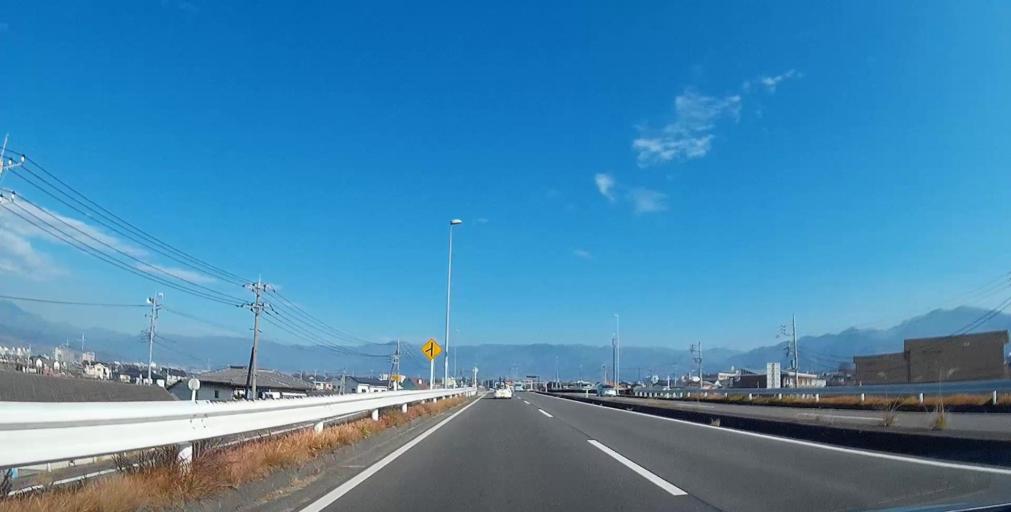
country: JP
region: Yamanashi
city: Isawa
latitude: 35.6442
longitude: 138.6507
